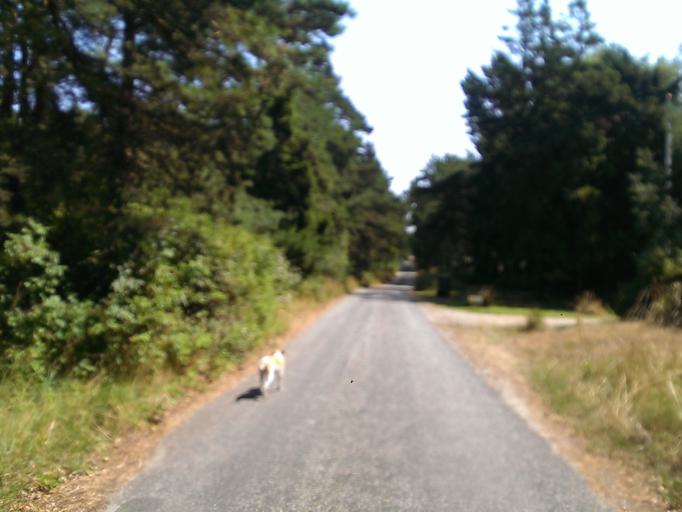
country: SE
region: Skane
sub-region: Simrishamns Kommun
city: Simrishamn
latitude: 55.4287
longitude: 14.2259
